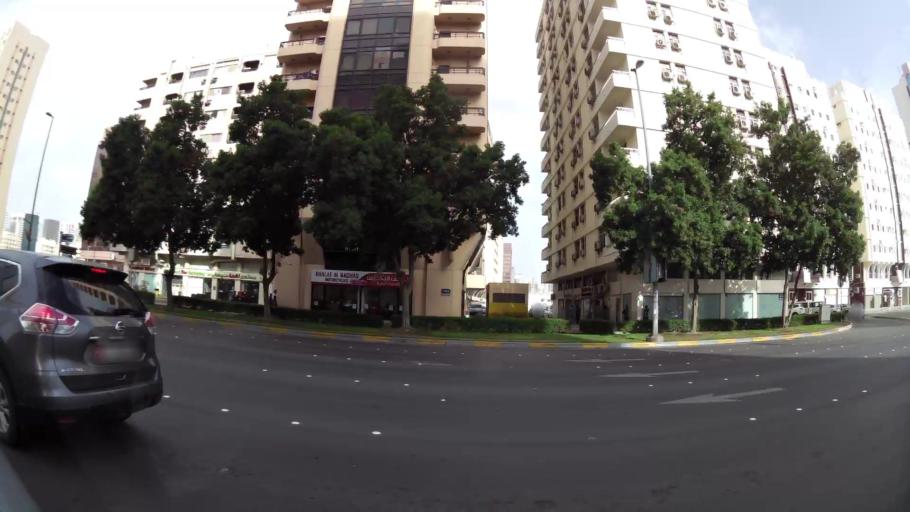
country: AE
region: Abu Dhabi
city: Abu Dhabi
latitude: 24.4798
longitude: 54.3704
